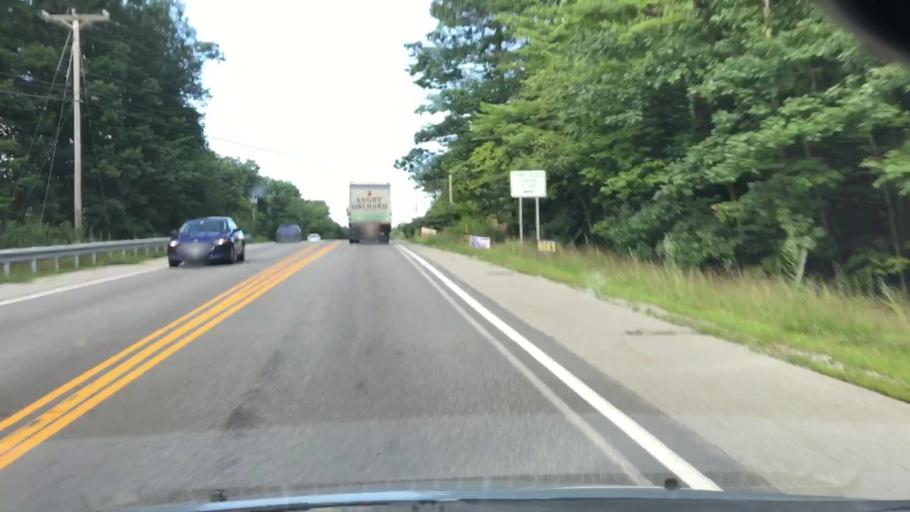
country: US
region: New Hampshire
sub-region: Hillsborough County
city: Bedford
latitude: 42.9081
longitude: -71.5685
